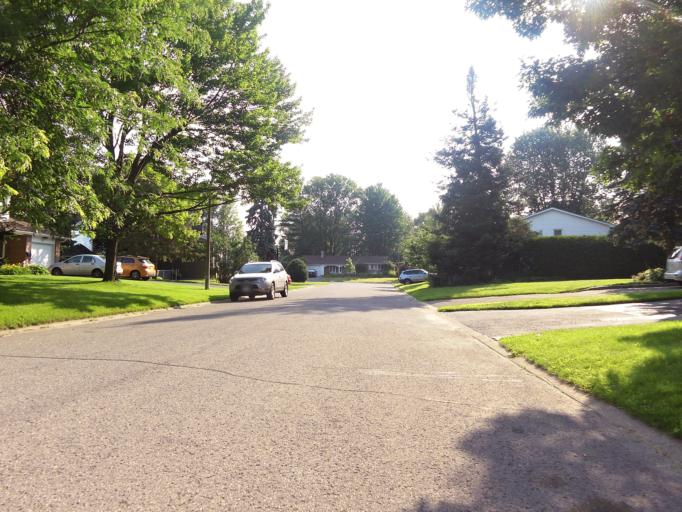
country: CA
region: Ontario
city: Bells Corners
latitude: 45.3365
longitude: -75.7808
